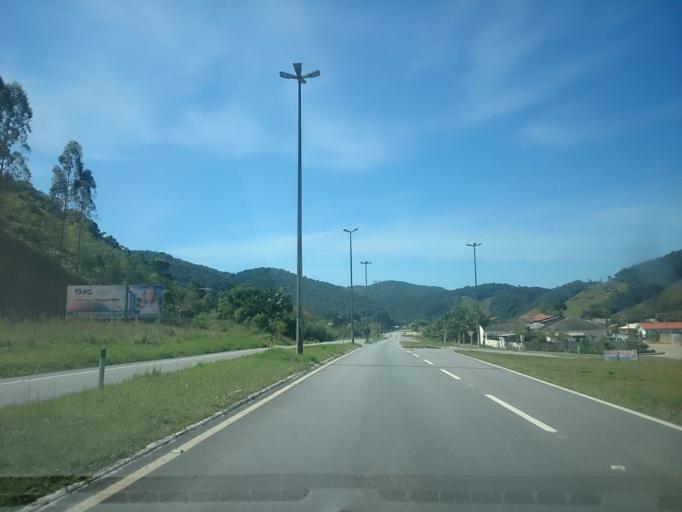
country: BR
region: Santa Catarina
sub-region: Santo Amaro Da Imperatriz
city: Santo Amaro da Imperatriz
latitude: -27.7189
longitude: -48.8839
